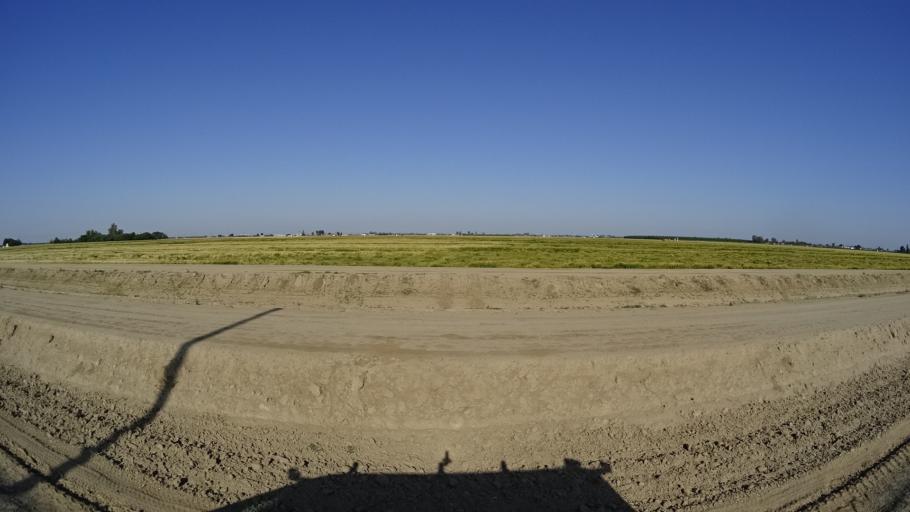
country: US
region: California
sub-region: Kings County
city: Home Garden
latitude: 36.3038
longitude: -119.5652
